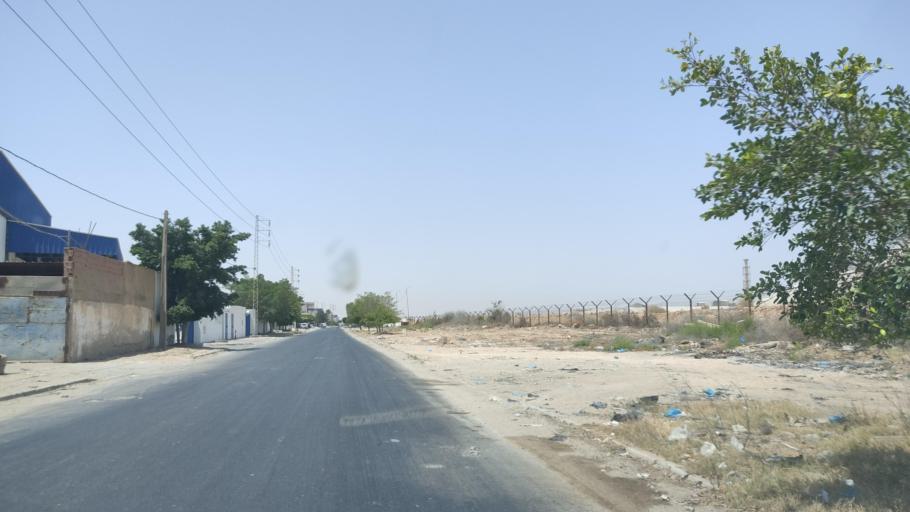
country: TN
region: Safaqis
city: Sfax
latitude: 34.6933
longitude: 10.7261
